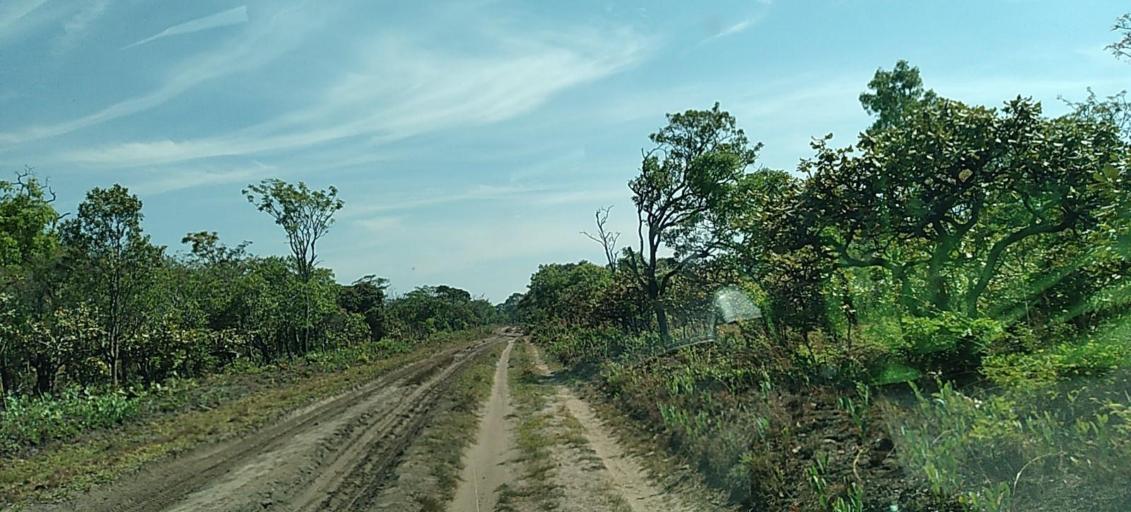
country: ZM
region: North-Western
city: Mwinilunga
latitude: -11.8002
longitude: 25.1664
